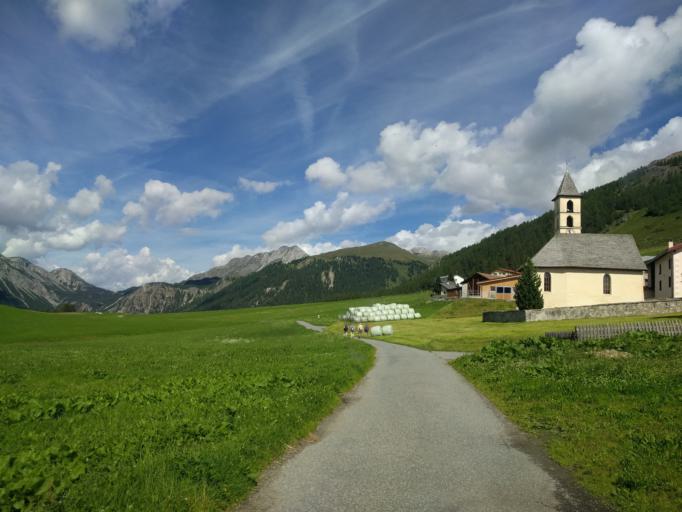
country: IT
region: Trentino-Alto Adige
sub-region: Bolzano
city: Tubre
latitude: 46.6219
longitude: 10.3695
